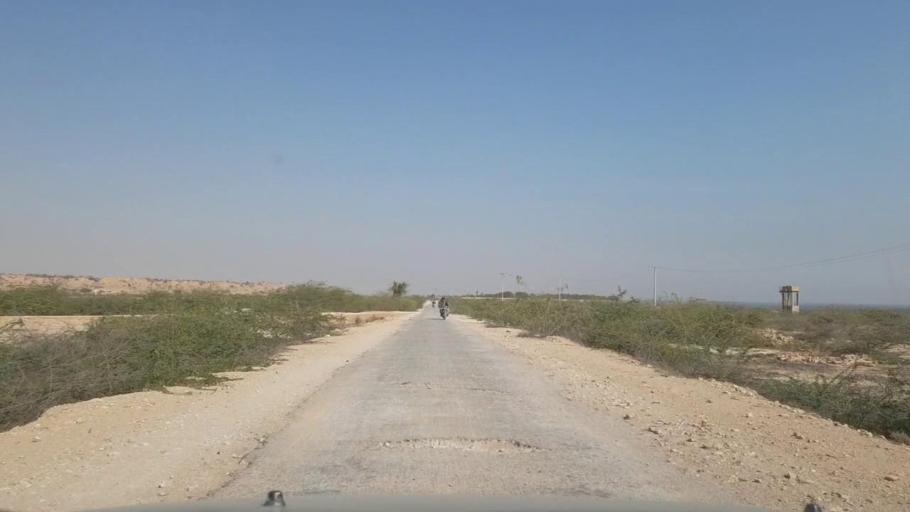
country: PK
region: Sindh
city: Thatta
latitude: 24.9858
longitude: 67.9978
